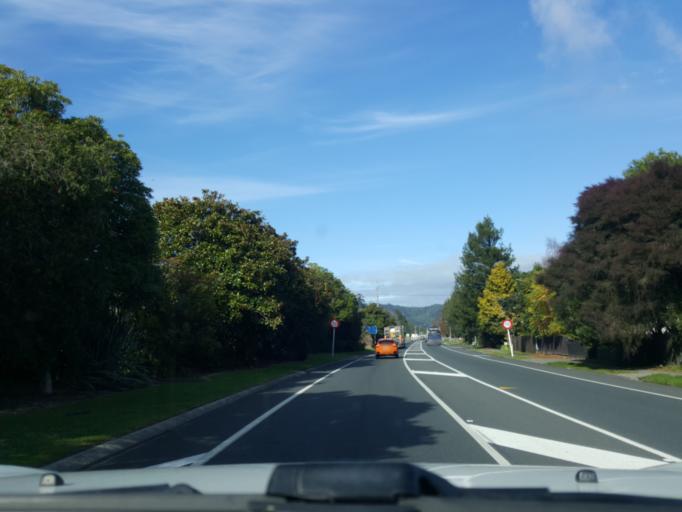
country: NZ
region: Waikato
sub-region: Waikato District
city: Ngaruawahia
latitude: -37.5736
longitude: 175.1593
